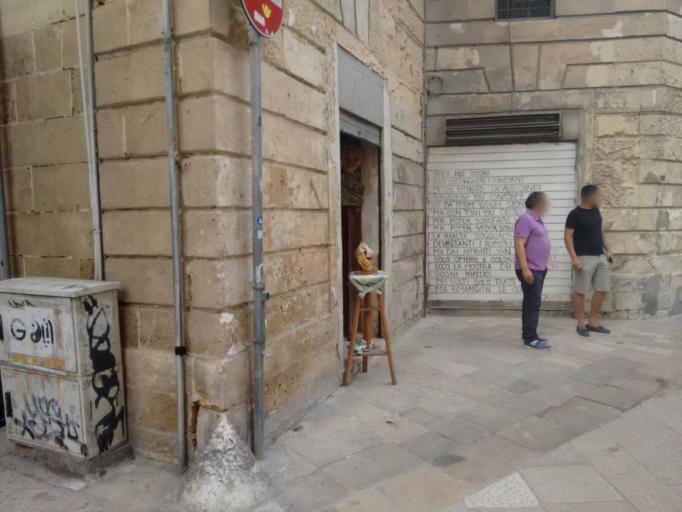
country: IT
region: Apulia
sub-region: Provincia di Lecce
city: Lecce
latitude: 40.3505
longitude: 18.1716
